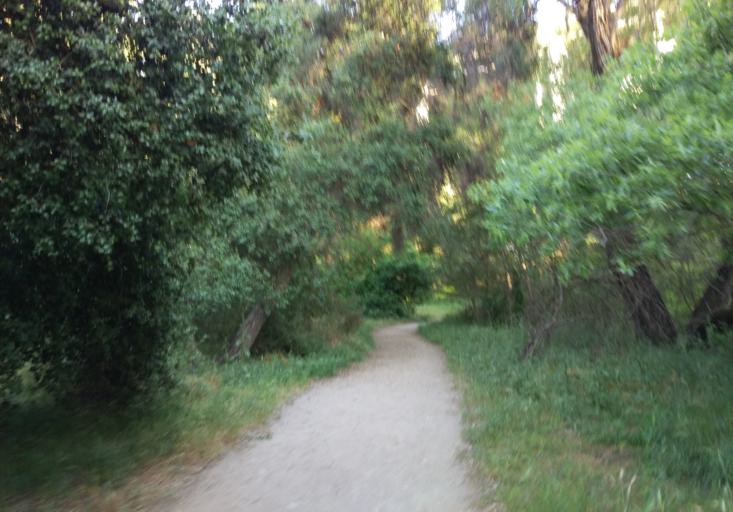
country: US
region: California
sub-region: Los Angeles County
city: Pasadena
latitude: 34.1468
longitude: -118.1649
